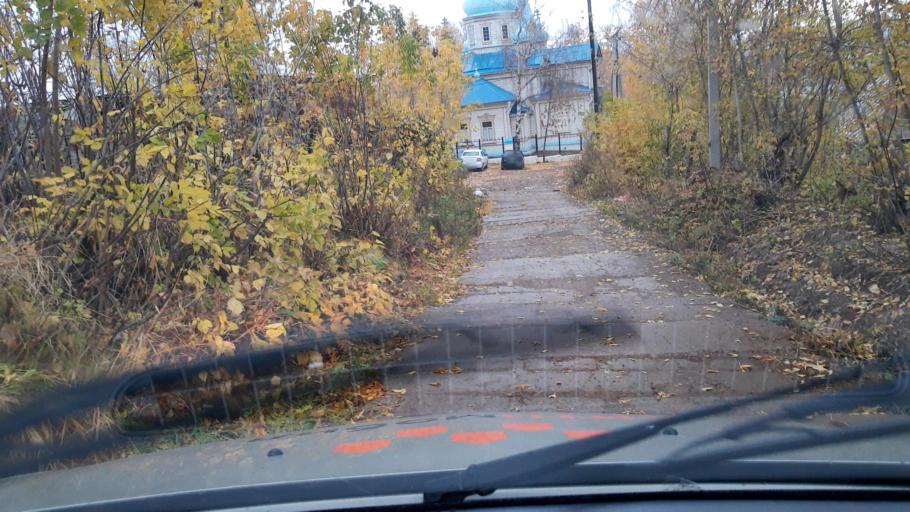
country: RU
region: Bashkortostan
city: Ufa
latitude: 54.7329
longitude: 55.9202
